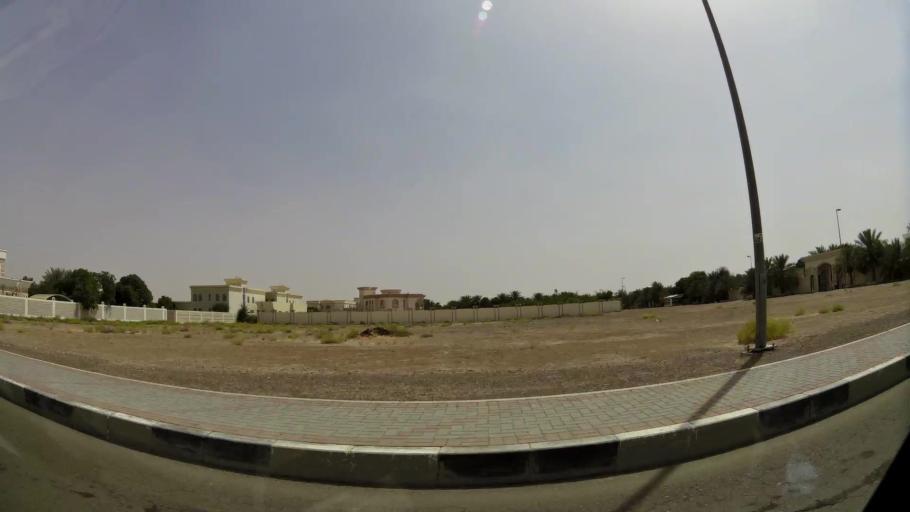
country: AE
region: Abu Dhabi
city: Al Ain
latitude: 24.1614
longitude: 55.6606
